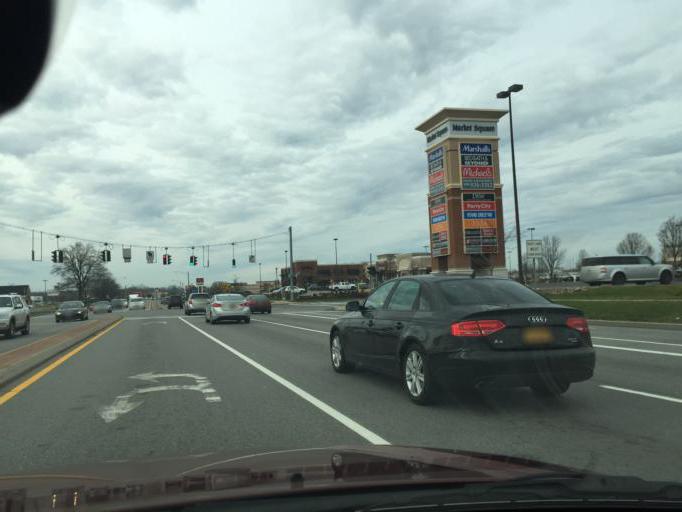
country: US
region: New York
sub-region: Monroe County
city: Rochester
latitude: 43.0871
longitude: -77.6239
